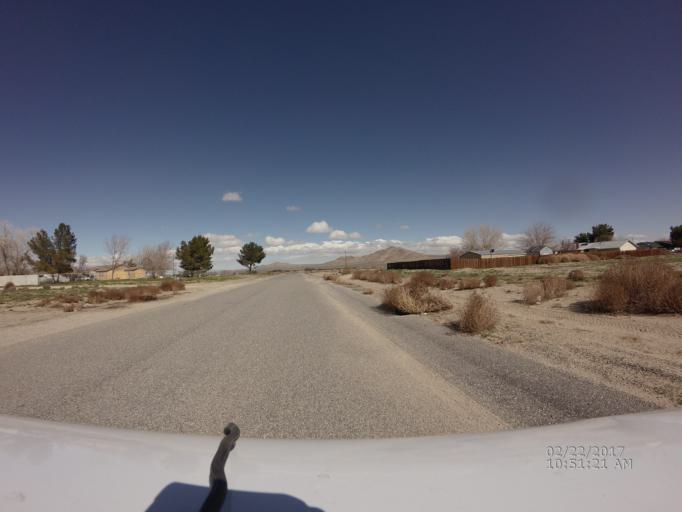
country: US
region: California
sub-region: Los Angeles County
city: Lake Los Angeles
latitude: 34.6300
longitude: -117.8183
